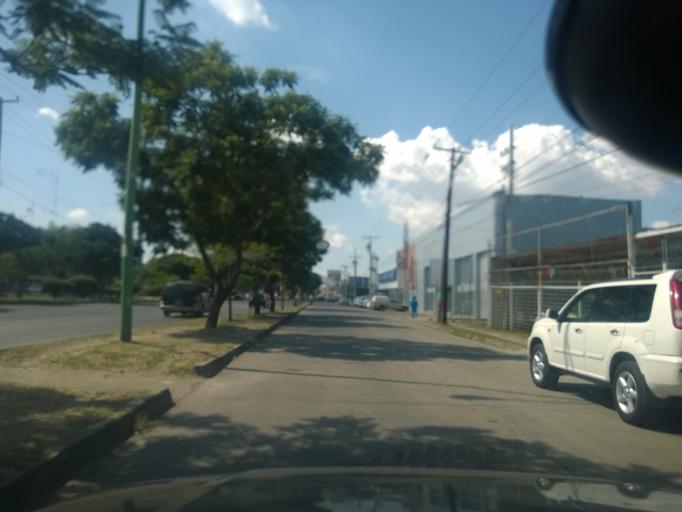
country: MX
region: Guanajuato
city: Leon
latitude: 21.1509
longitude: -101.6681
